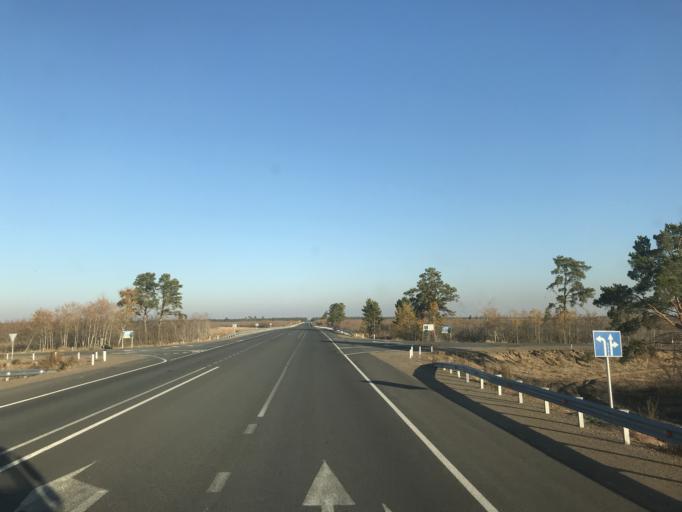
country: KZ
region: Pavlodar
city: Kurchatov
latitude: 51.1030
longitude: 78.9953
